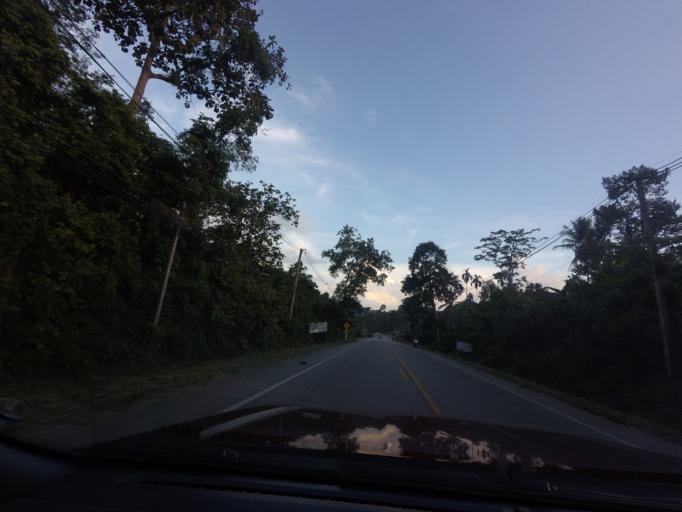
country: TH
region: Yala
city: Than To
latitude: 6.1238
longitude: 101.1919
